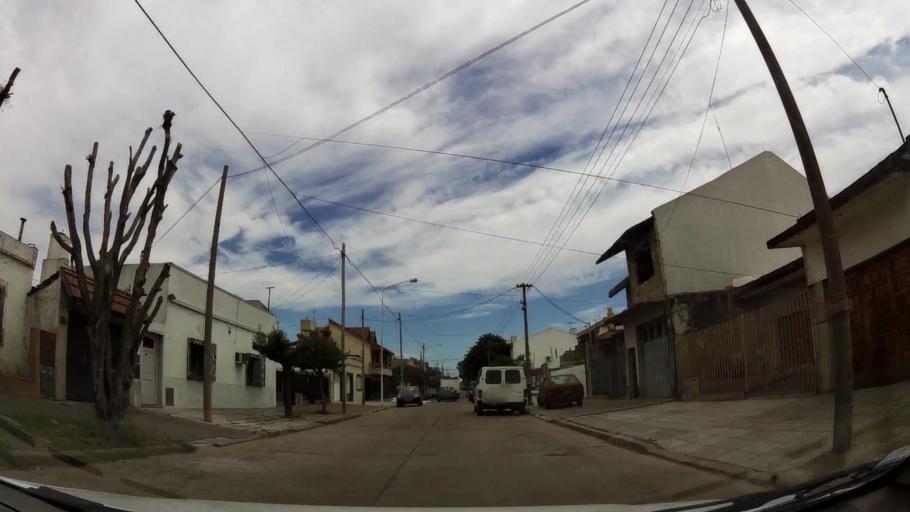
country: AR
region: Buenos Aires
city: San Justo
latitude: -34.6682
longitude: -58.5490
